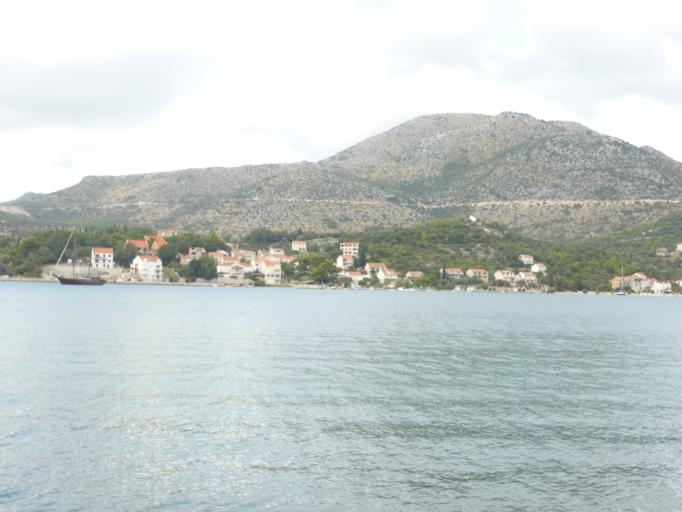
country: HR
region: Dubrovacko-Neretvanska
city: Podgora
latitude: 42.7805
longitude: 17.8868
